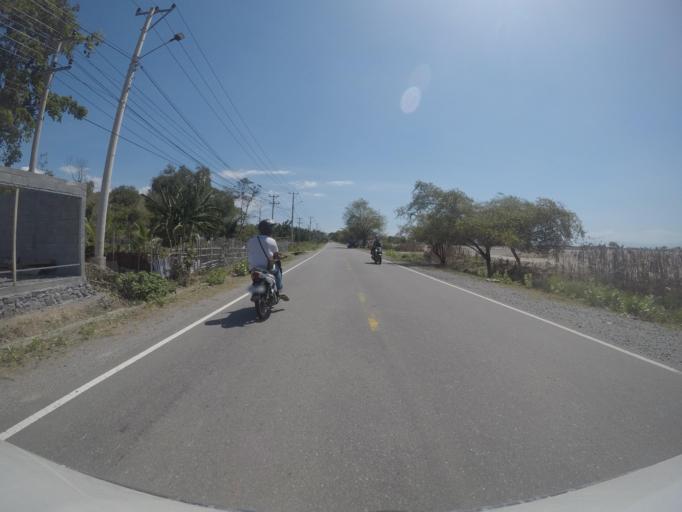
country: TL
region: Liquica
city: Liquica
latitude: -8.5787
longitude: 125.3648
